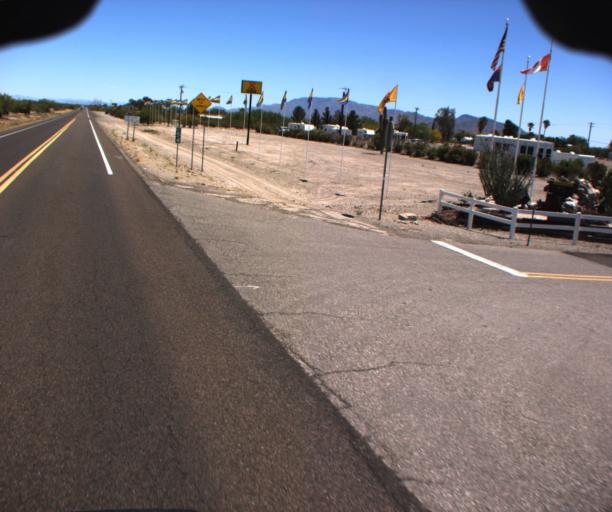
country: US
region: Arizona
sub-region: La Paz County
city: Salome
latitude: 33.7619
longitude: -113.6504
